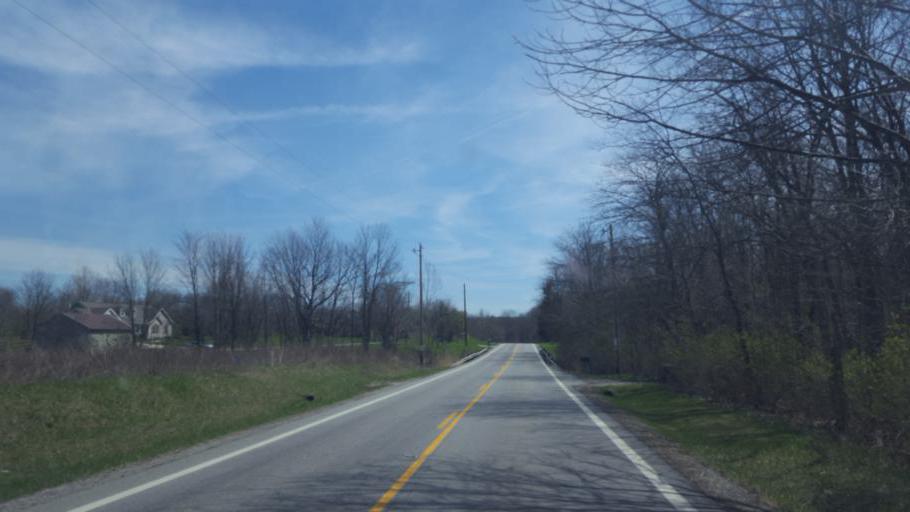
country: US
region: Ohio
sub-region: Delaware County
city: Ashley
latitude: 40.4181
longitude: -83.0254
